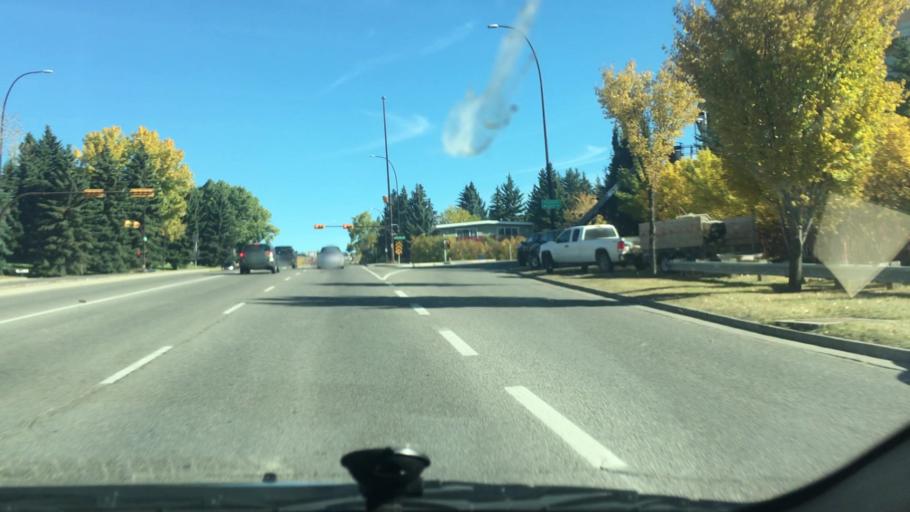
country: CA
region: Alberta
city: Calgary
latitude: 51.1073
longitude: -114.1628
